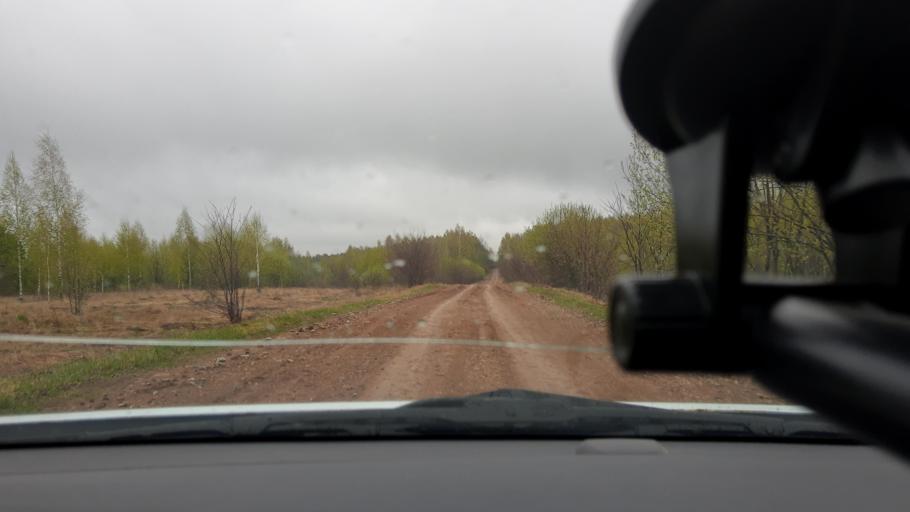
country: RU
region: Bashkortostan
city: Pavlovka
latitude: 55.4365
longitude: 56.3608
